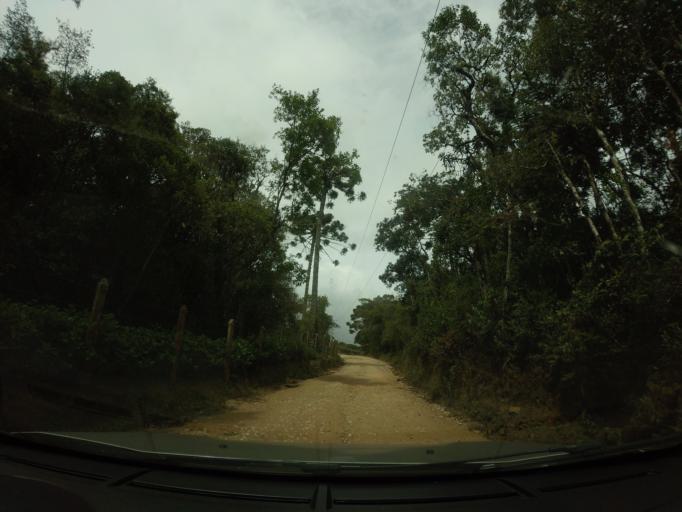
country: BR
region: Sao Paulo
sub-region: Campos Do Jordao
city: Campos do Jordao
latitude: -22.6767
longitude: -45.6476
